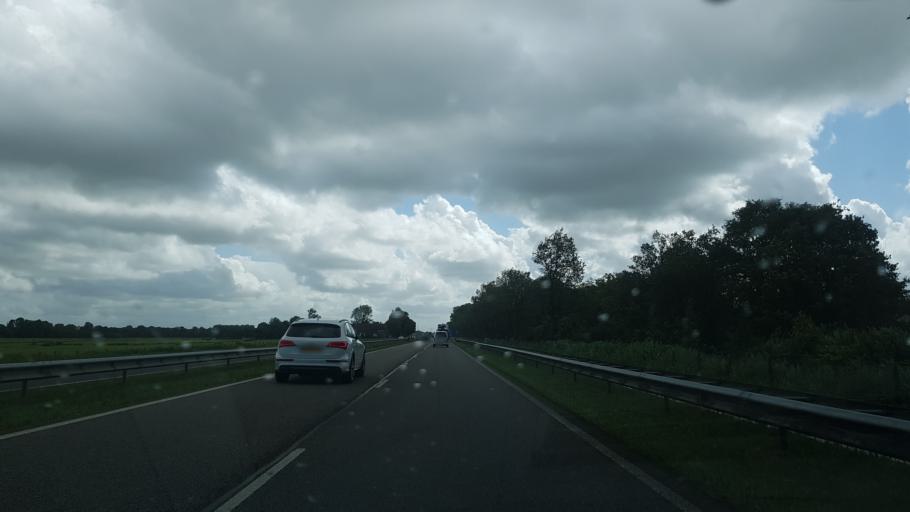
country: NL
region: Friesland
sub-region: Gemeente Tytsjerksteradiel
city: Tytsjerk
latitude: 53.2179
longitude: 5.8953
